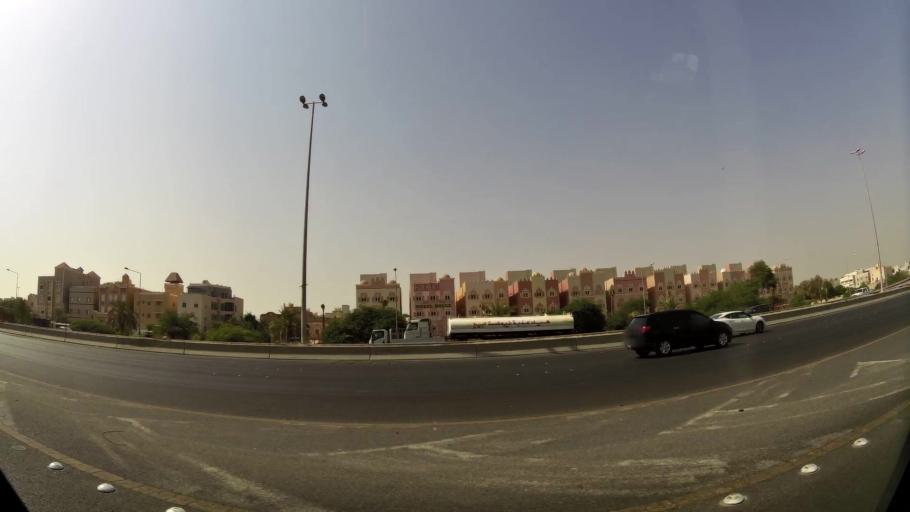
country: KW
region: Al Ahmadi
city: Al Fintas
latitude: 29.1816
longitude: 48.1134
